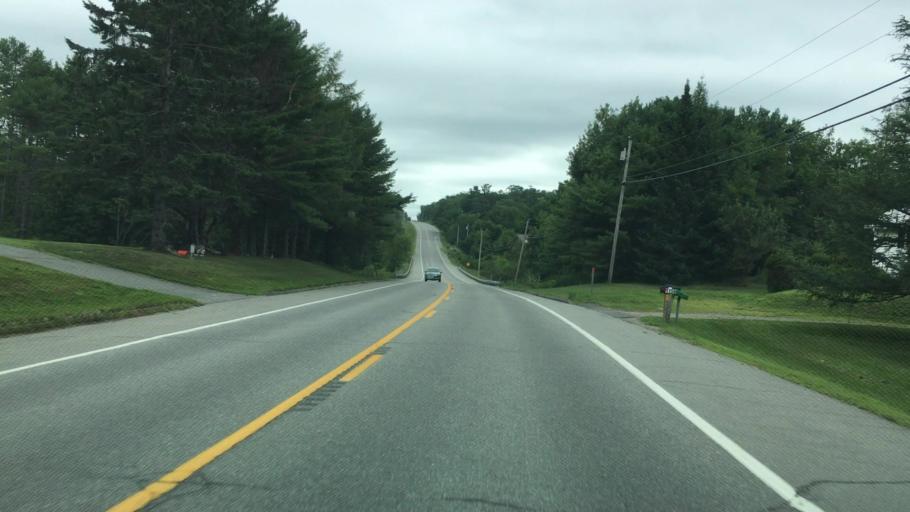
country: US
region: Maine
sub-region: Waldo County
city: Winterport
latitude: 44.6669
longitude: -68.8322
